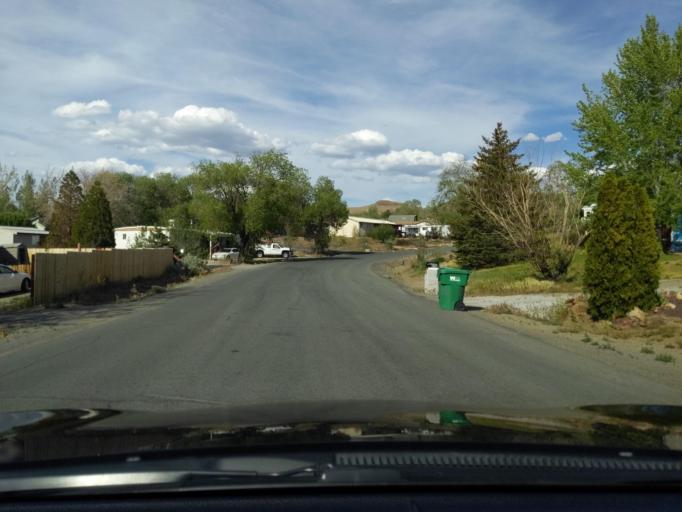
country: US
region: Nevada
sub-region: Washoe County
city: Sun Valley
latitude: 39.5785
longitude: -119.7750
